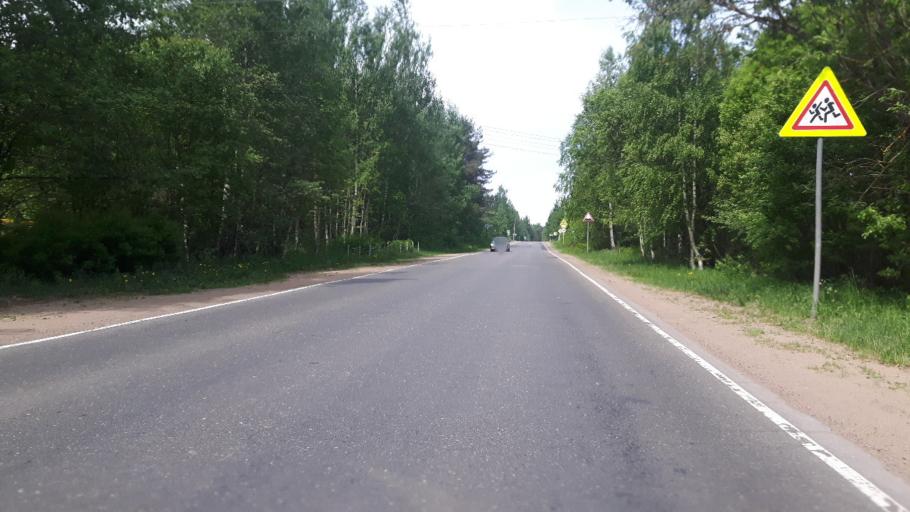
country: RU
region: Leningrad
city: Ust'-Luga
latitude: 59.6439
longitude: 28.2713
